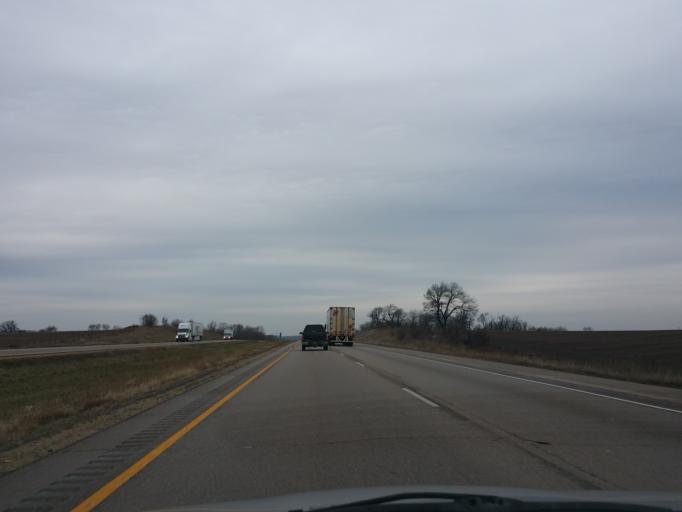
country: US
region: Wisconsin
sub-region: Dane County
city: Deerfield
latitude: 42.9727
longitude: -89.1129
